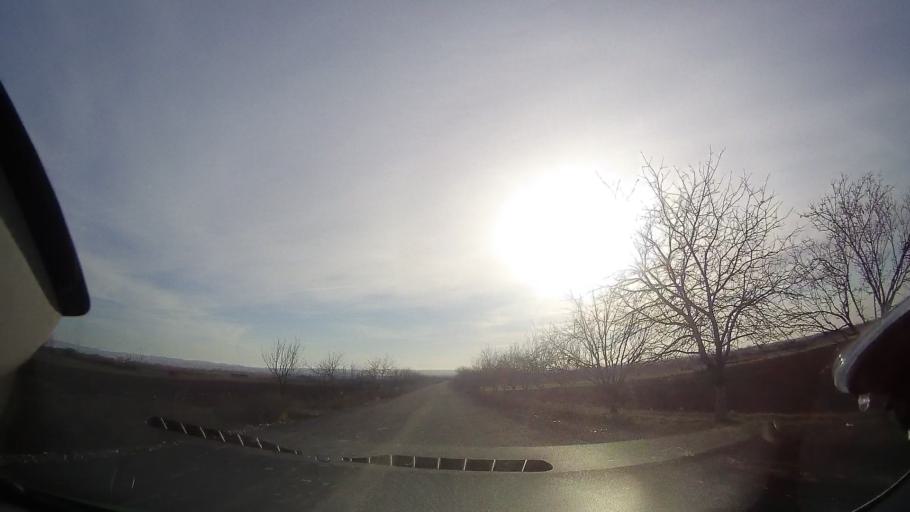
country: RO
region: Bihor
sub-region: Comuna Tileagd
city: Tileagd
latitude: 47.0919
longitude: 22.1780
